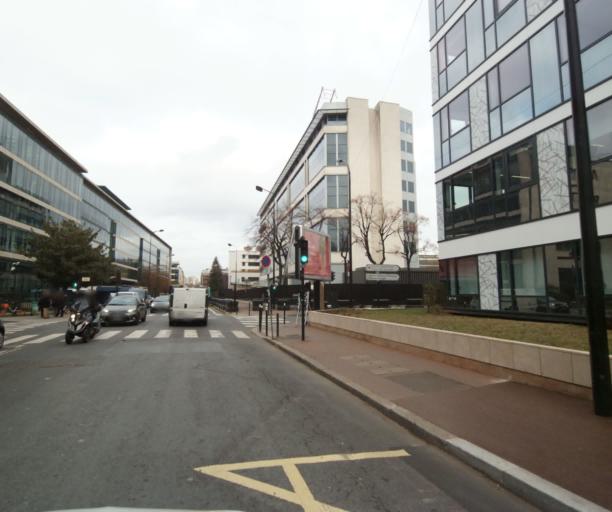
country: FR
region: Ile-de-France
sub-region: Departement des Hauts-de-Seine
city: Levallois-Perret
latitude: 48.8917
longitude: 2.2781
